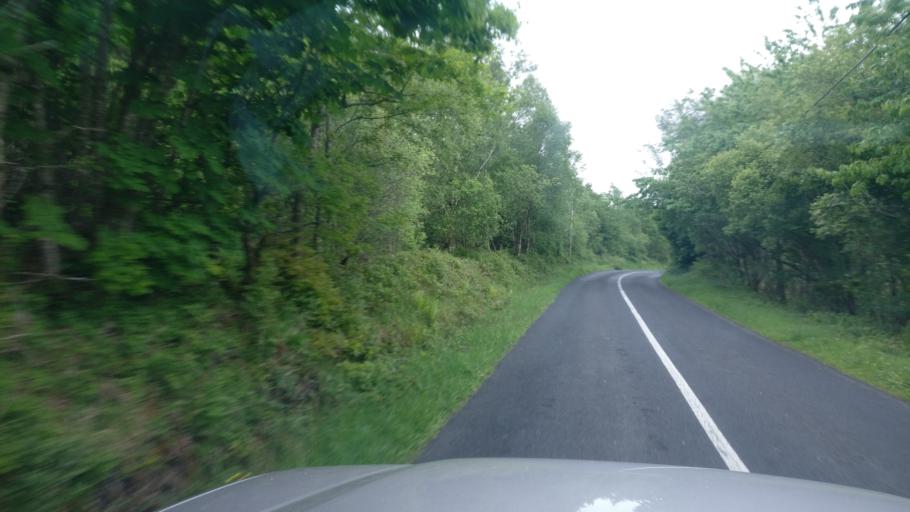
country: IE
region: Connaught
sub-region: County Galway
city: Gort
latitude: 53.0588
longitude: -8.6646
